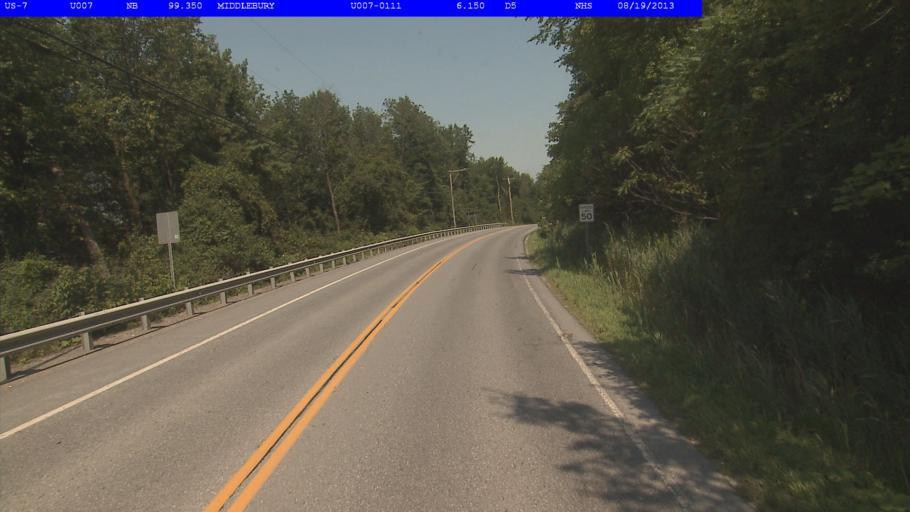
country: US
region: Vermont
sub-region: Addison County
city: Middlebury (village)
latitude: 44.0291
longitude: -73.1676
